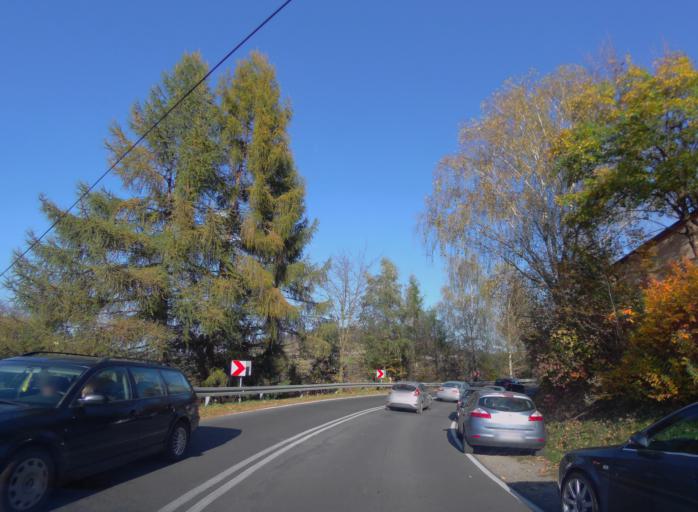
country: PL
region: Subcarpathian Voivodeship
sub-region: Powiat leski
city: Polanczyk
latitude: 49.4013
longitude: 22.4488
